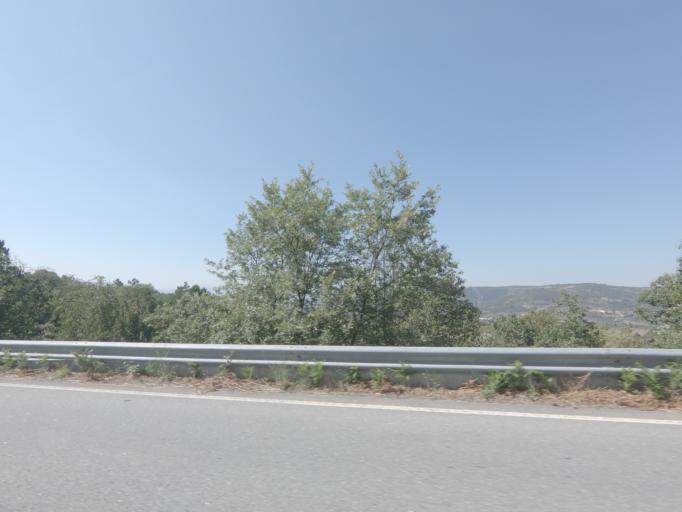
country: PT
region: Viseu
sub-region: Tarouca
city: Tarouca
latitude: 41.0395
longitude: -7.7372
